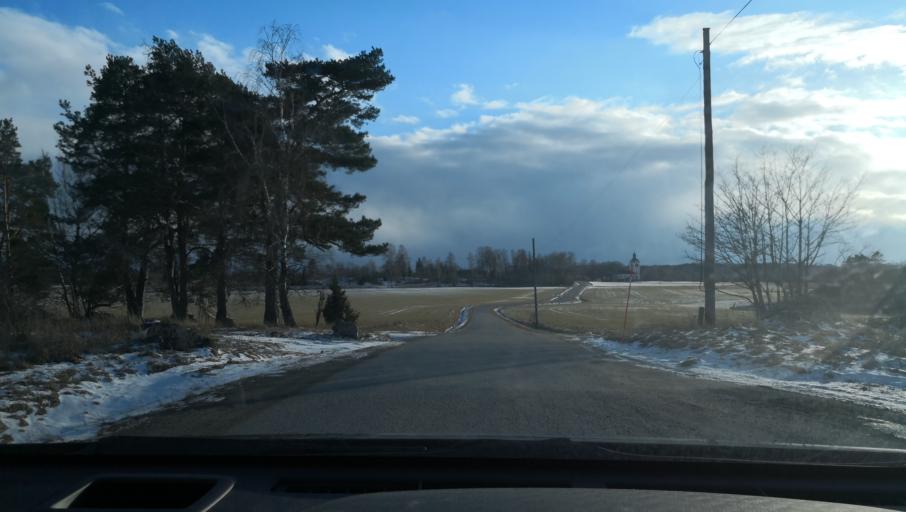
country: SE
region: Uppsala
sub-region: Enkopings Kommun
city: Irsta
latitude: 59.6877
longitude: 16.8576
